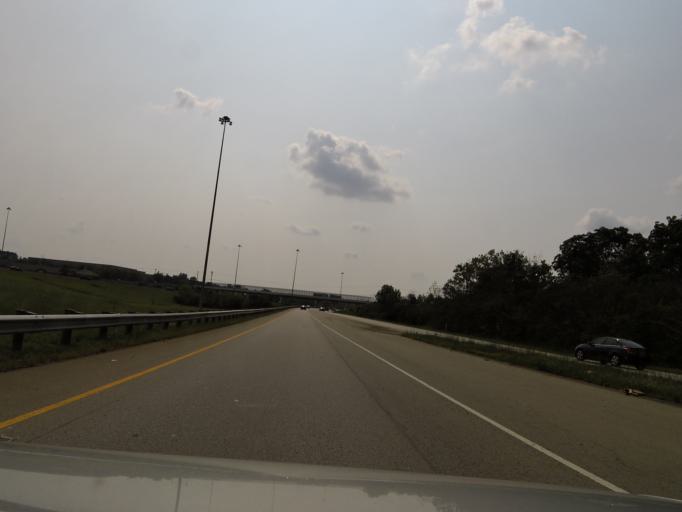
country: US
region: Ohio
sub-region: Hamilton County
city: Glendale
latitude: 39.2920
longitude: -84.4421
